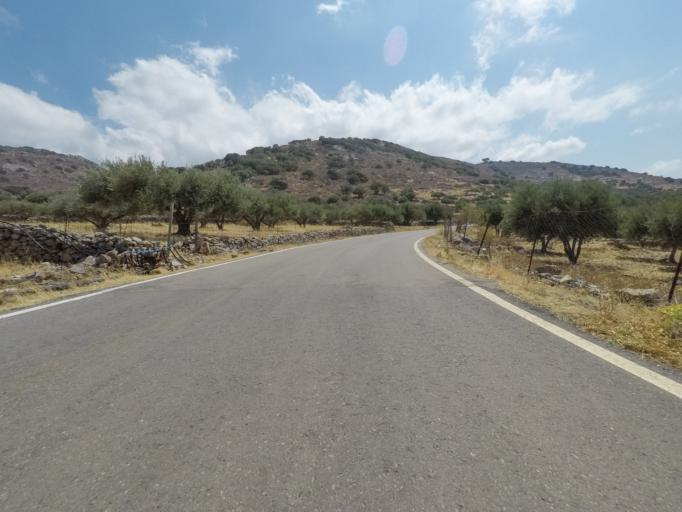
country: GR
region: Crete
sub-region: Nomos Lasithiou
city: Elounda
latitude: 35.3181
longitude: 25.6887
